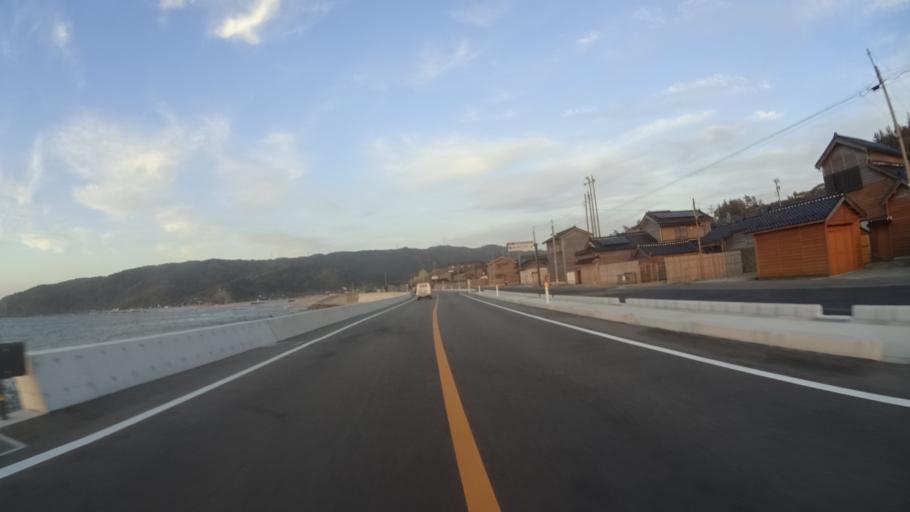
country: JP
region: Ishikawa
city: Nanao
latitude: 37.2822
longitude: 136.7340
